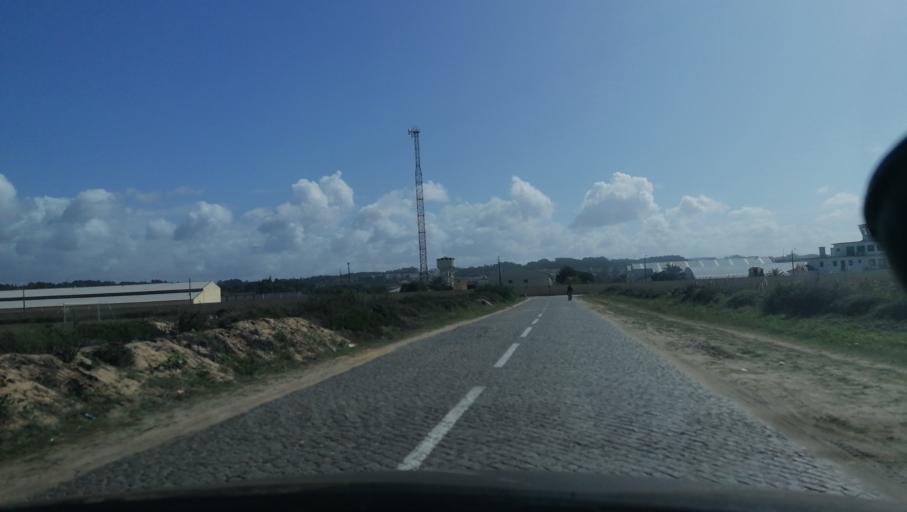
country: PT
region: Aveiro
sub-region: Espinho
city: Souto
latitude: 40.9773
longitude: -8.6452
